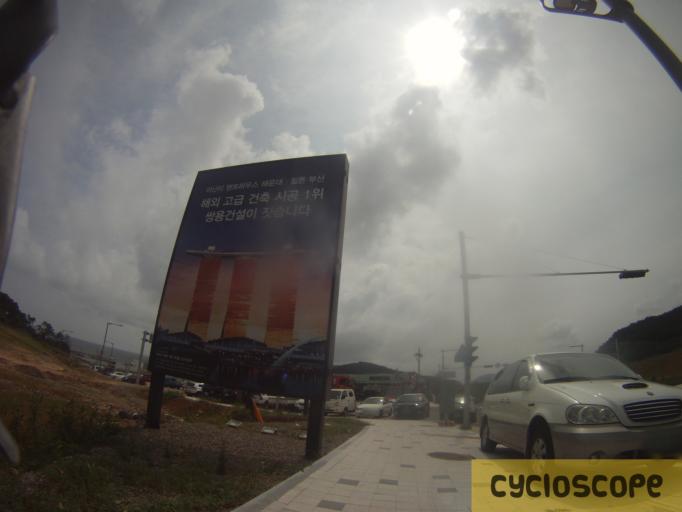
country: KR
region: Busan
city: Kijang
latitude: 35.1963
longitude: 129.2223
